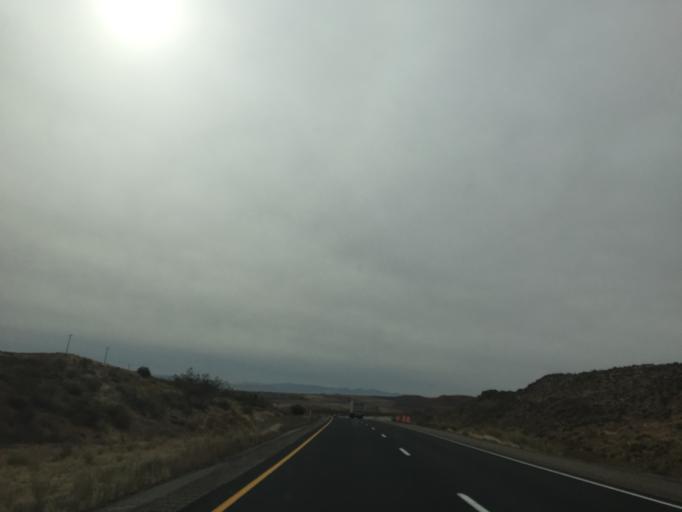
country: US
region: Utah
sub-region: Washington County
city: Hurricane
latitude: 37.2201
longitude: -113.3855
